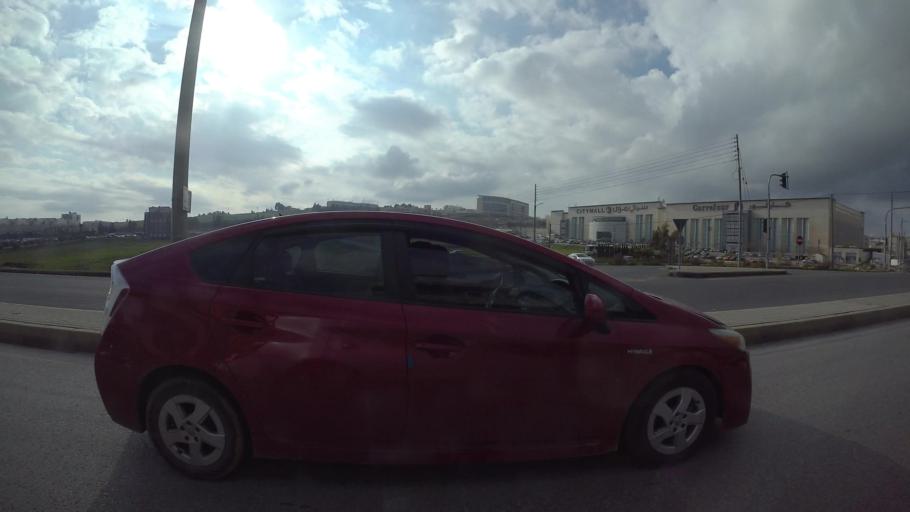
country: JO
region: Amman
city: Wadi as Sir
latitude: 31.9787
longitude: 35.8405
